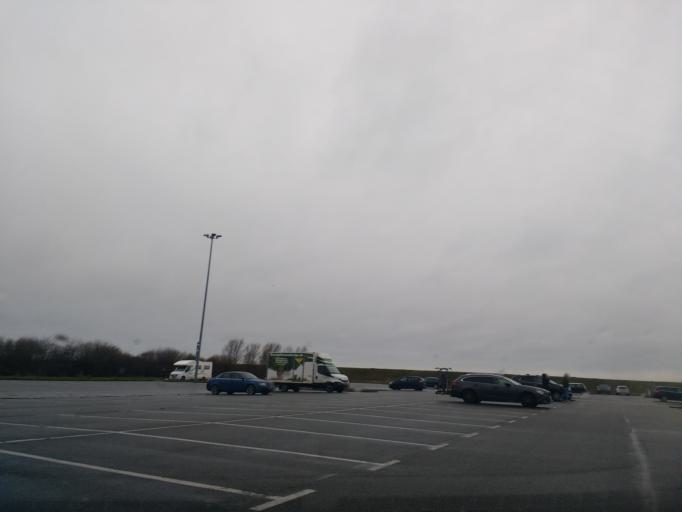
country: DE
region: Schleswig-Holstein
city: Fehmarn
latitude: 54.5022
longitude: 11.2230
